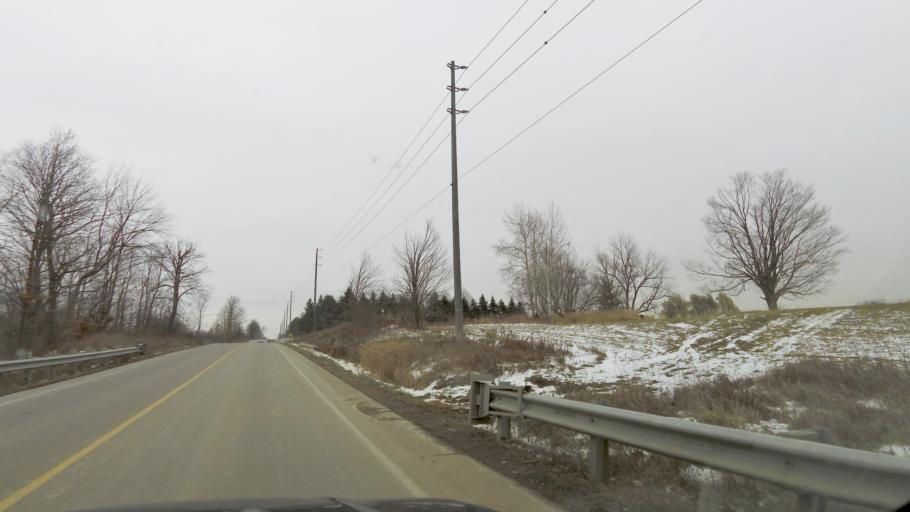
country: CA
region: Ontario
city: Vaughan
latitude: 43.8713
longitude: -79.6173
